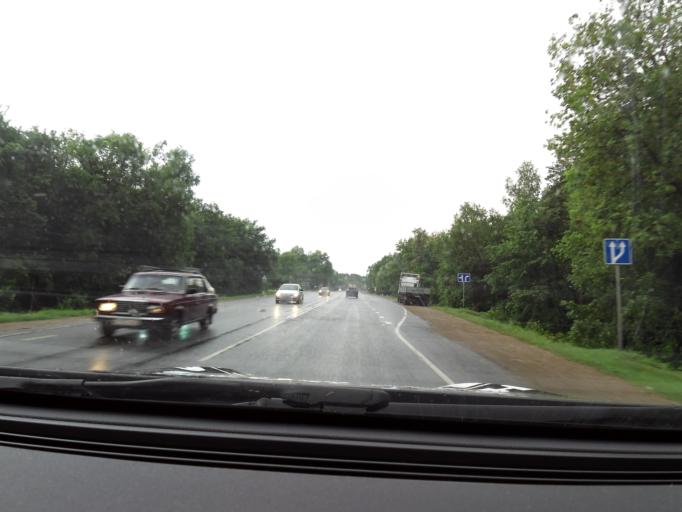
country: RU
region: Bashkortostan
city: Mikhaylovka
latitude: 54.8376
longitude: 55.7989
